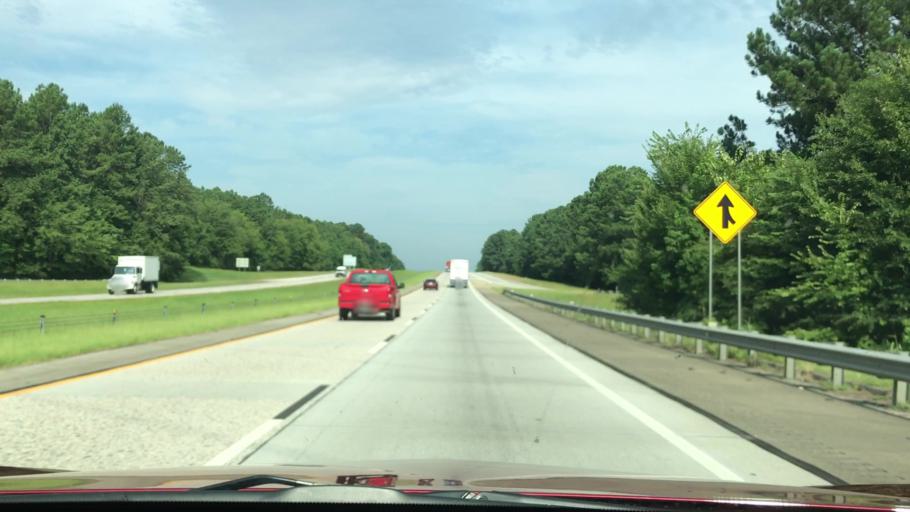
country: US
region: Georgia
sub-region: Columbia County
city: Appling
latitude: 33.4971
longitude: -82.3172
